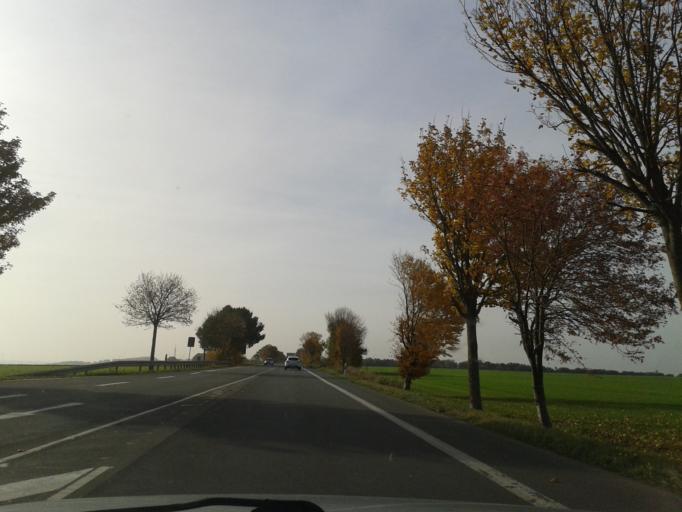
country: DE
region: North Rhine-Westphalia
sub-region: Regierungsbezirk Detmold
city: Buren
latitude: 51.5881
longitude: 8.5726
